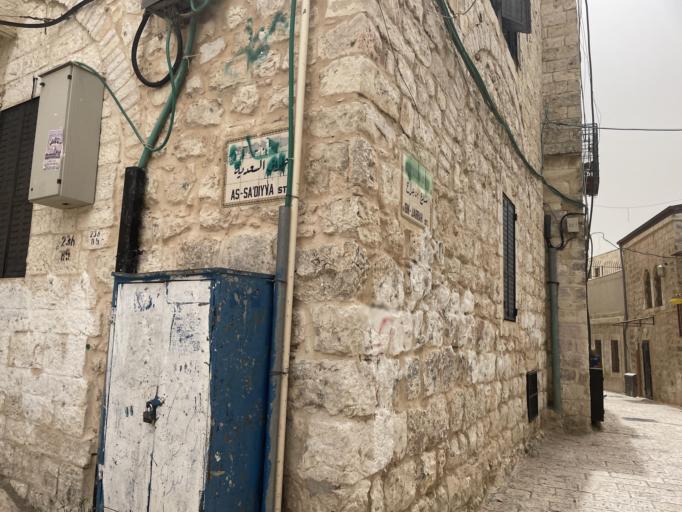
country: PS
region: West Bank
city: East Jerusalem
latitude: 31.7821
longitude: 35.2314
